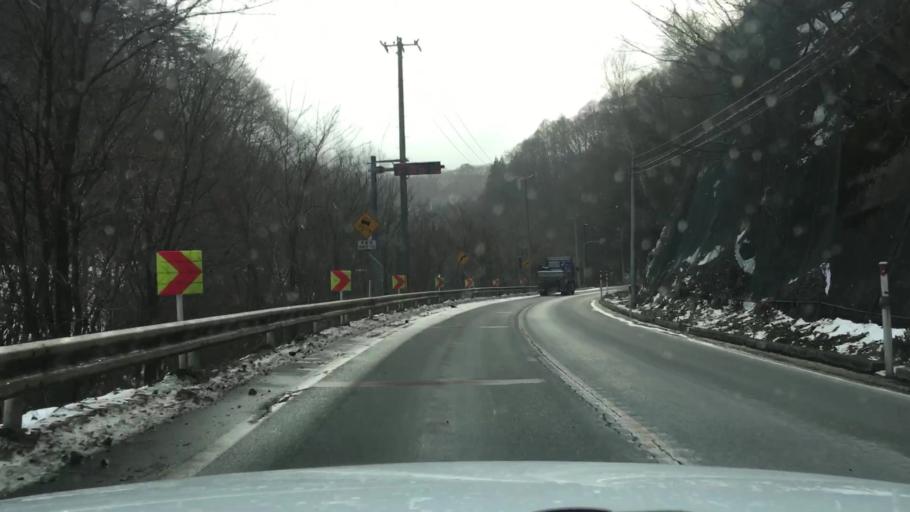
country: JP
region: Iwate
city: Tono
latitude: 39.6154
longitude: 141.4872
